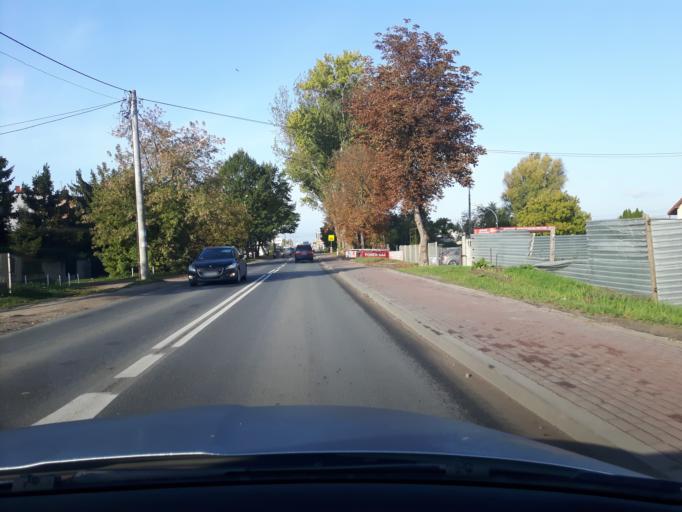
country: PL
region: Masovian Voivodeship
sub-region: Powiat wolominski
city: Zabki
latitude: 52.2860
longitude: 21.1022
